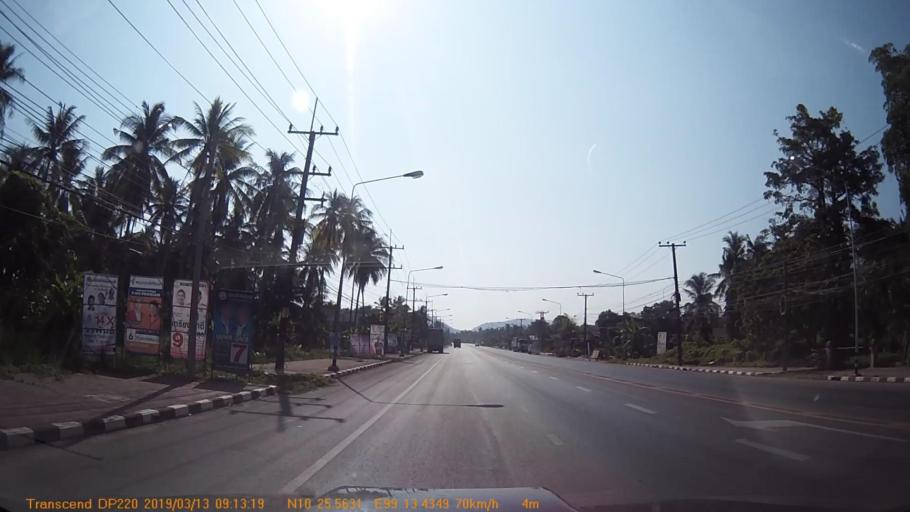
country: TH
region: Chumphon
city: Chumphon
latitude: 10.4259
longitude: 99.2242
